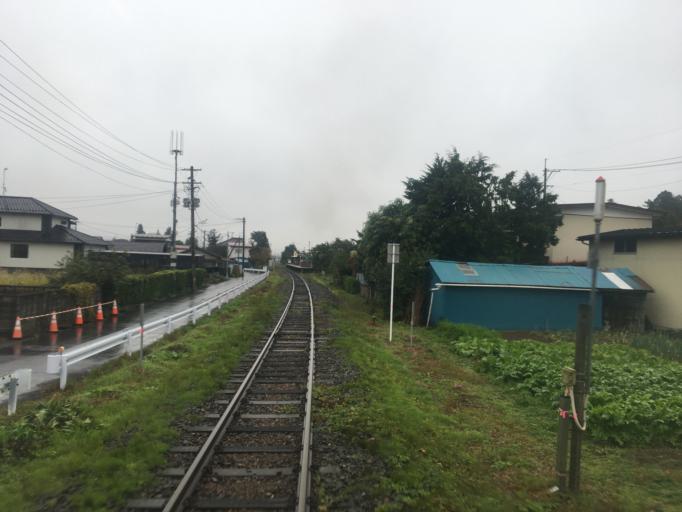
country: JP
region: Miyagi
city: Furukawa
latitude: 38.6591
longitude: 140.8623
